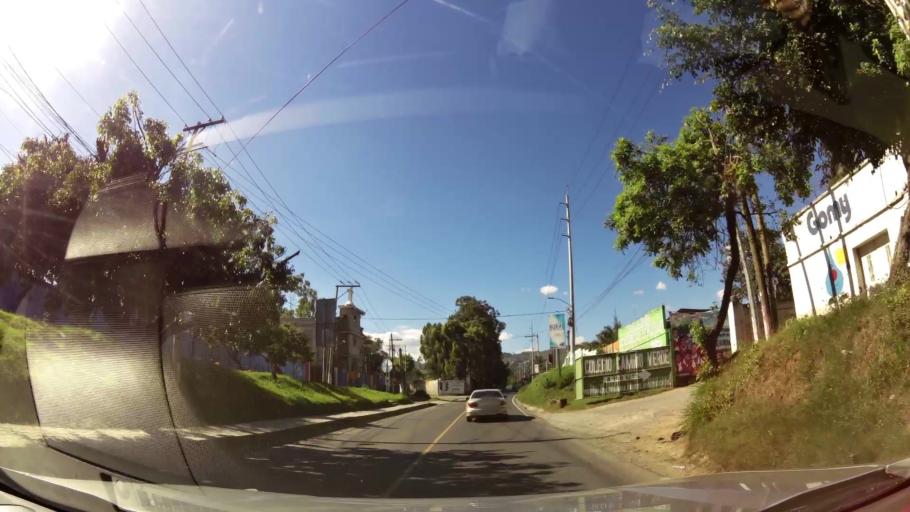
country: GT
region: Guatemala
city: Villa Nueva
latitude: 14.5364
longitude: -90.6044
